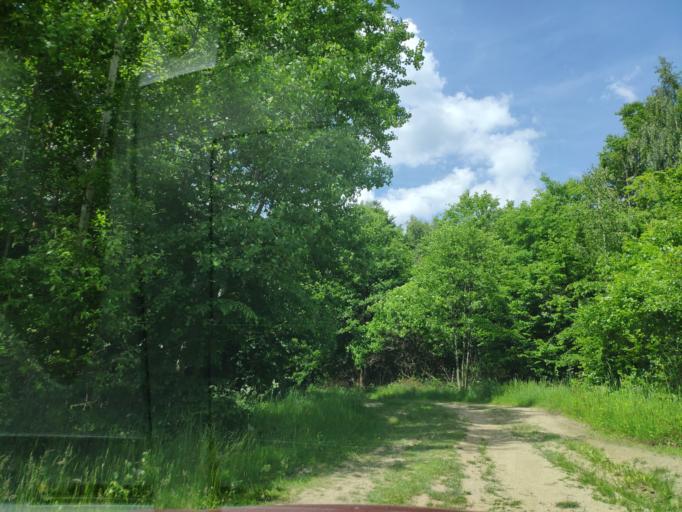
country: SK
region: Kosicky
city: Medzev
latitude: 48.7234
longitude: 20.9584
